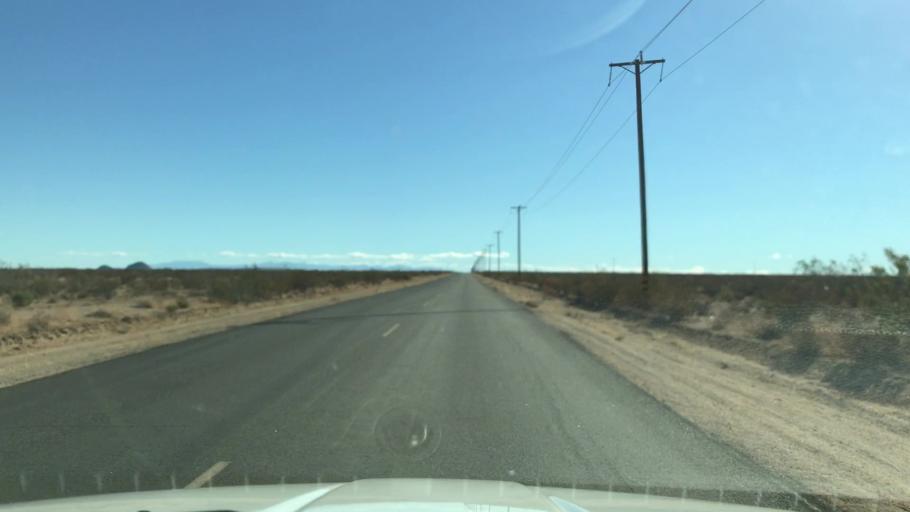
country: US
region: California
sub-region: Kern County
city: California City
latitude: 35.1901
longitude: -117.9858
